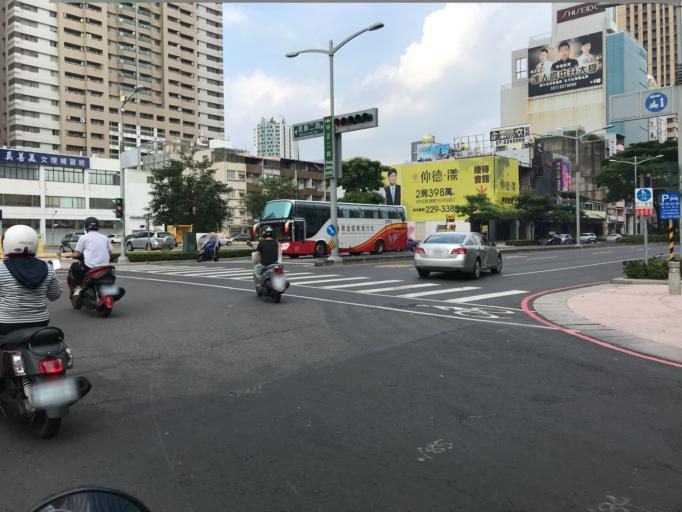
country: TW
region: Kaohsiung
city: Kaohsiung
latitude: 22.6303
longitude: 120.3136
